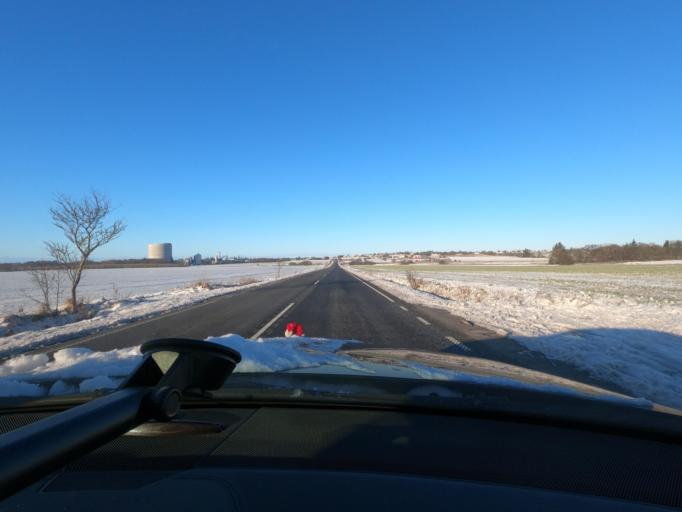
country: DK
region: South Denmark
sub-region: Tonder Kommune
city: Toftlund
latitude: 55.1691
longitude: 9.0730
